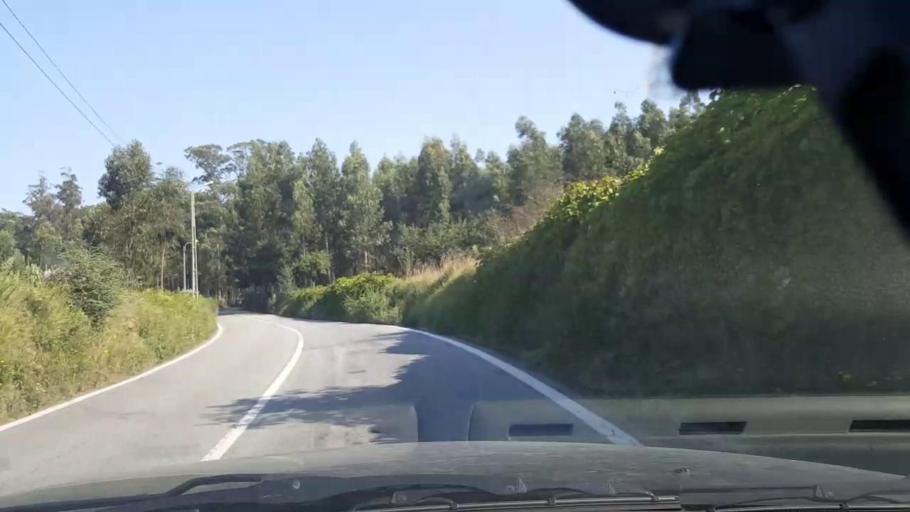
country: PT
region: Porto
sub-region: Maia
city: Gemunde
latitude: 41.2912
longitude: -8.6828
